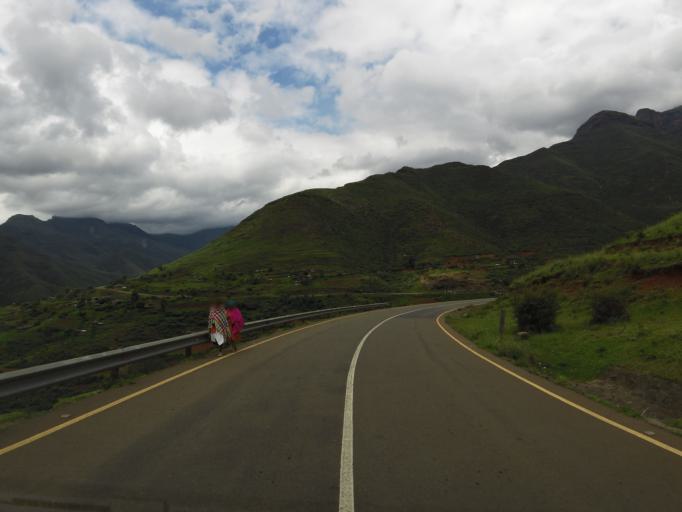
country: LS
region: Butha-Buthe
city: Butha-Buthe
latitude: -29.0439
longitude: 28.3096
